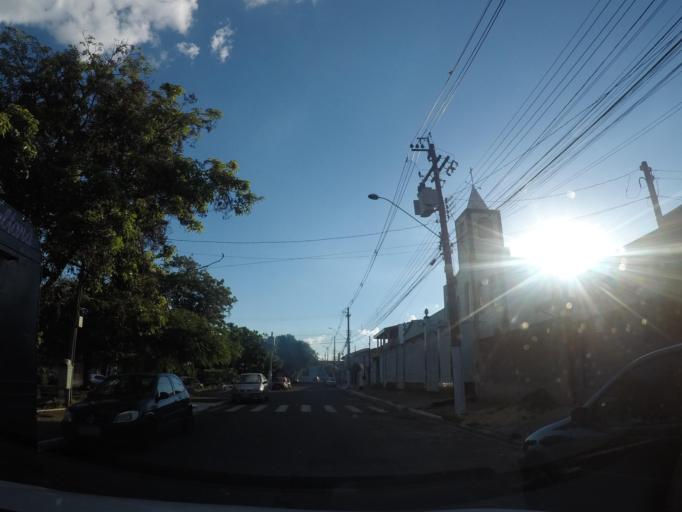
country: BR
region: Sao Paulo
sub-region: Sumare
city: Sumare
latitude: -22.8121
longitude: -47.2407
